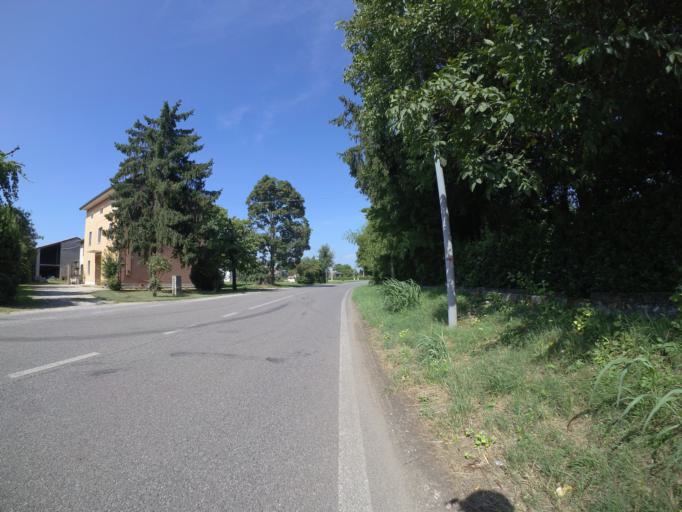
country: IT
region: Friuli Venezia Giulia
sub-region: Provincia di Udine
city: Talmassons
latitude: 45.9339
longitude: 13.1242
